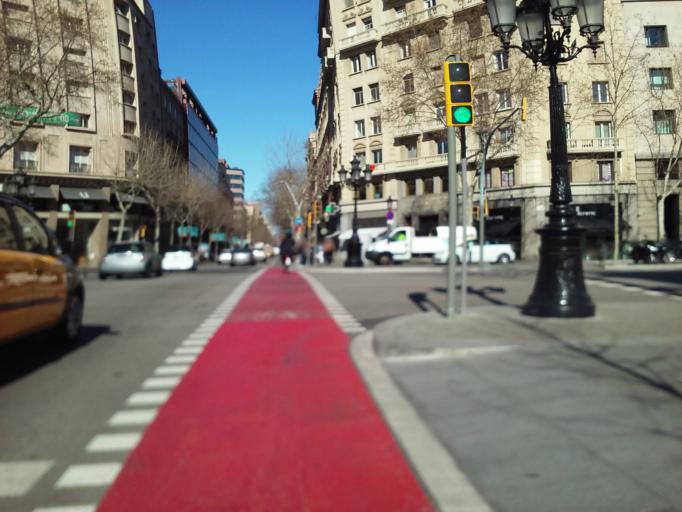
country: ES
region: Catalonia
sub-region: Provincia de Barcelona
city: Eixample
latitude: 41.3911
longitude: 2.1658
